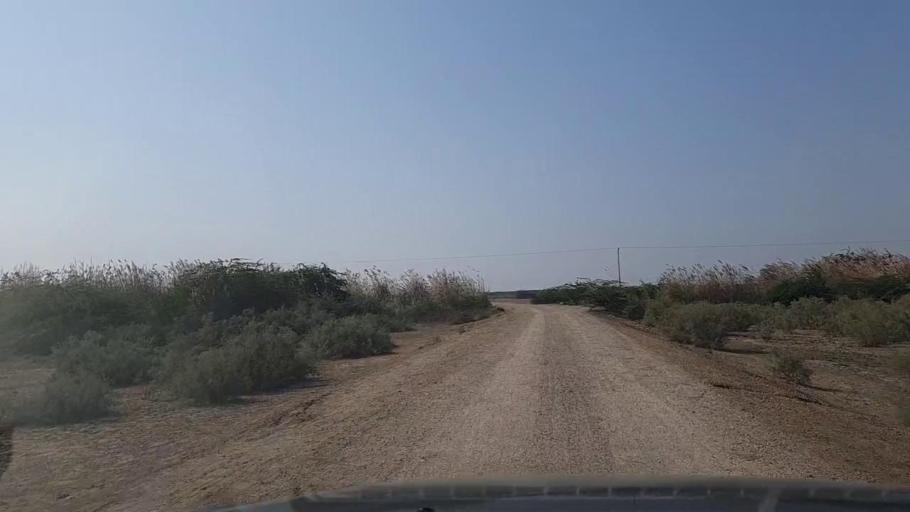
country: PK
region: Sindh
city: Mirpur Sakro
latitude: 24.4260
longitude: 67.7101
